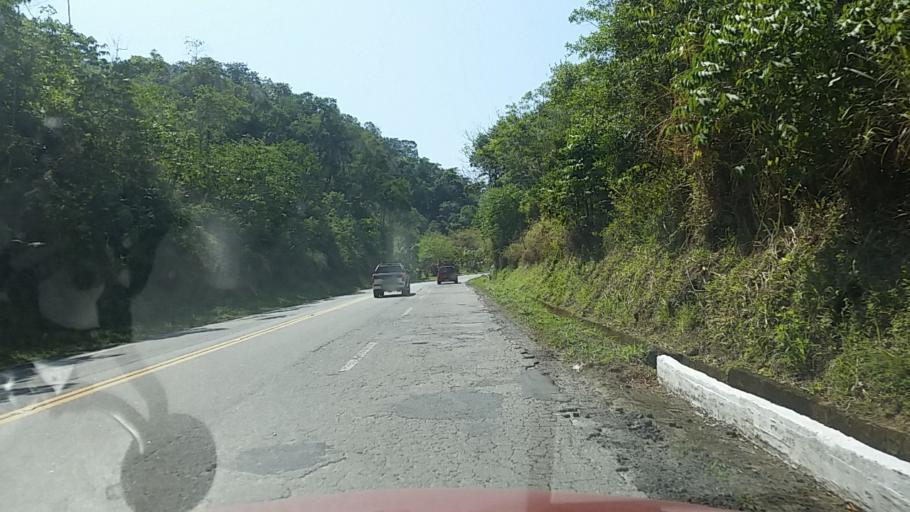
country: BR
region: Sao Paulo
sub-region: Miracatu
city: Miracatu
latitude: -24.3807
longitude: -47.5033
